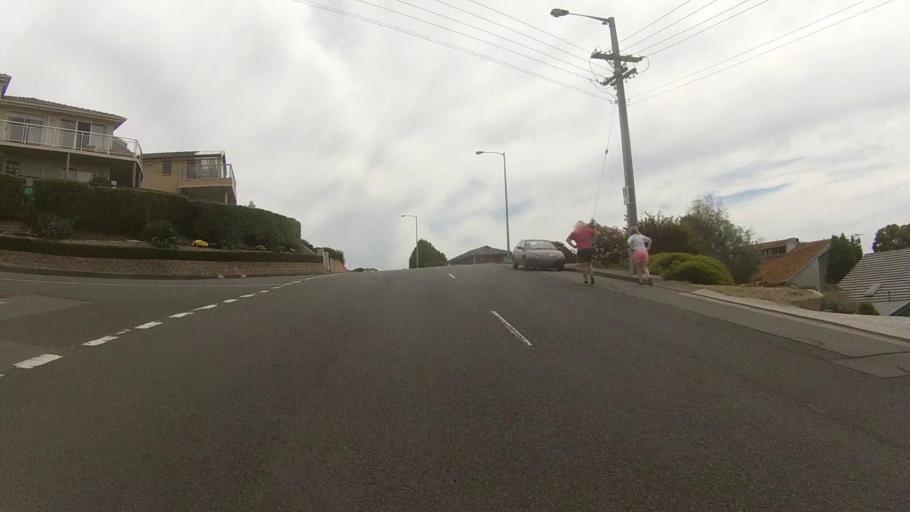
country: AU
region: Tasmania
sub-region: Kingborough
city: Taroona
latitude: -42.9191
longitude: 147.3528
